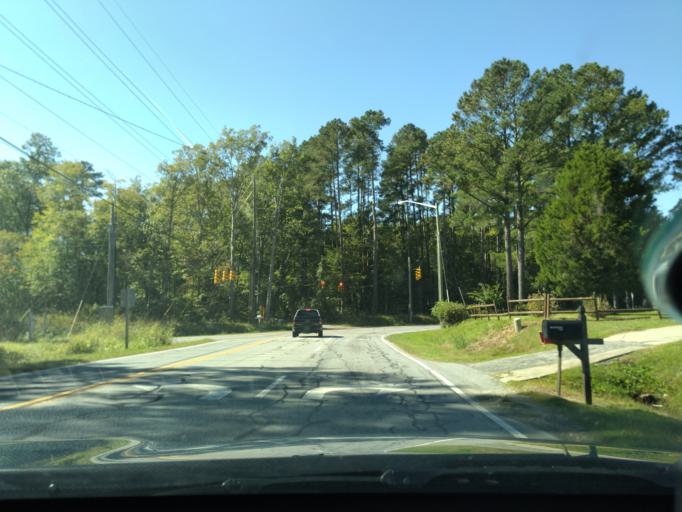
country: US
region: North Carolina
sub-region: Beaufort County
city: Washington
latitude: 35.5537
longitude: -77.0166
